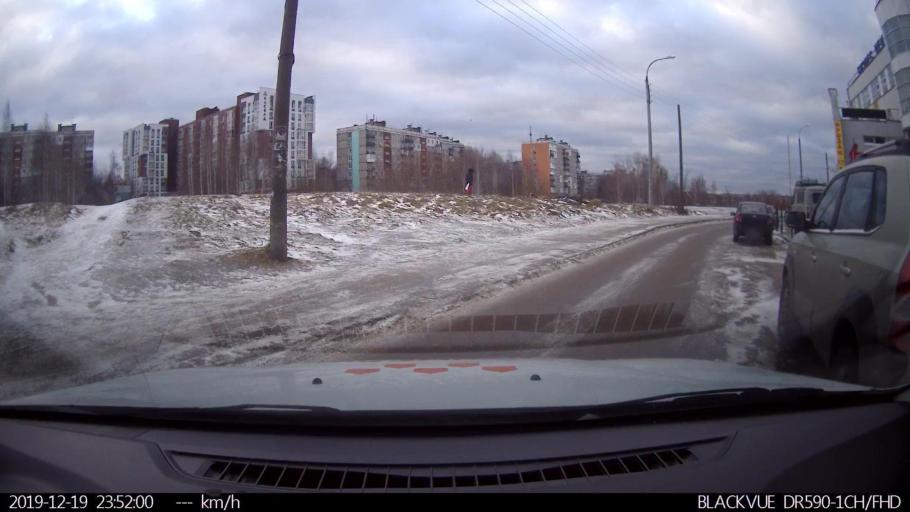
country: RU
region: Vologda
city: Molochnoye
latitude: 58.9980
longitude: 39.4797
